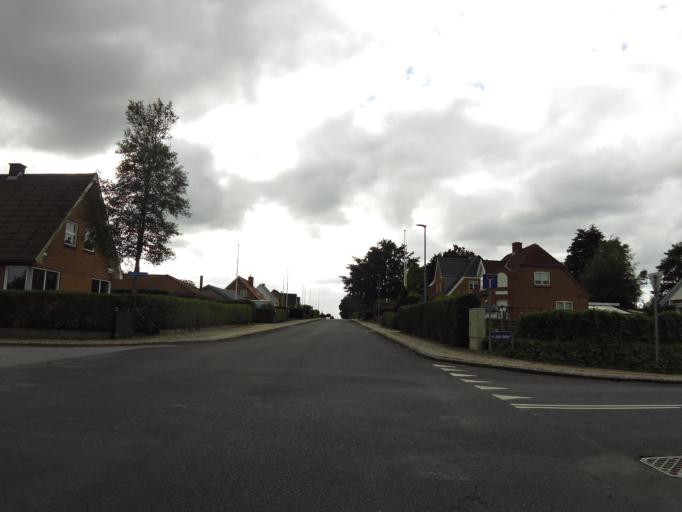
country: DK
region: South Denmark
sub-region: Kolding Kommune
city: Vamdrup
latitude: 55.3565
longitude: 9.1952
